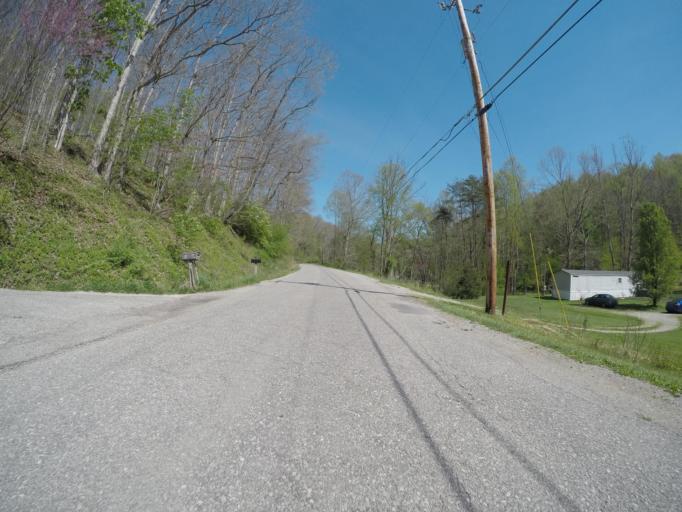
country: US
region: West Virginia
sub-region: Kanawha County
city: Charleston
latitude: 38.4161
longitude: -81.5789
